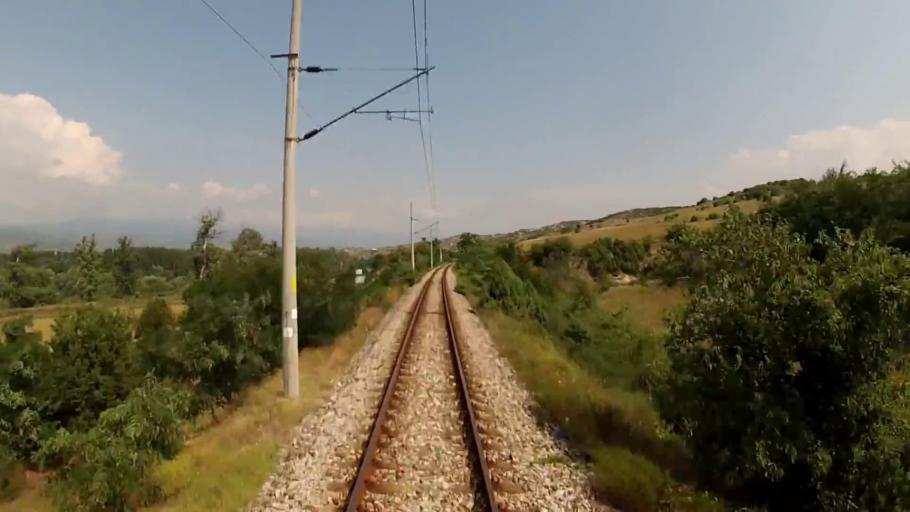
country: BG
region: Blagoevgrad
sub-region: Obshtina Strumyani
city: Strumyani
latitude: 41.6156
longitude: 23.2203
